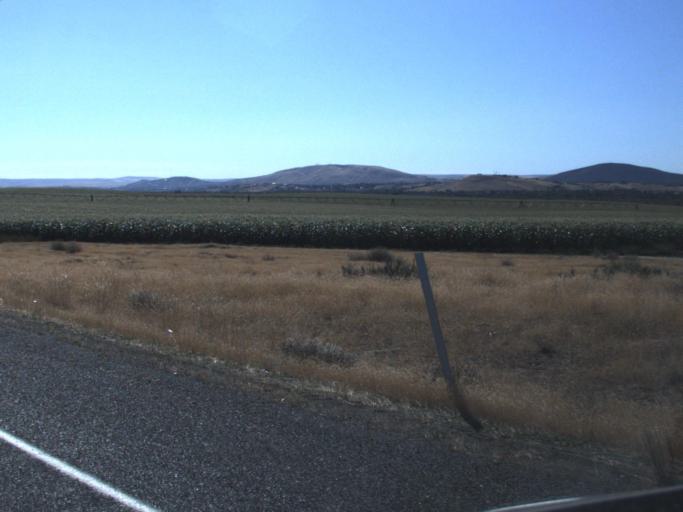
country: US
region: Washington
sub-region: Benton County
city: West Richland
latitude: 46.3513
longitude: -119.3642
